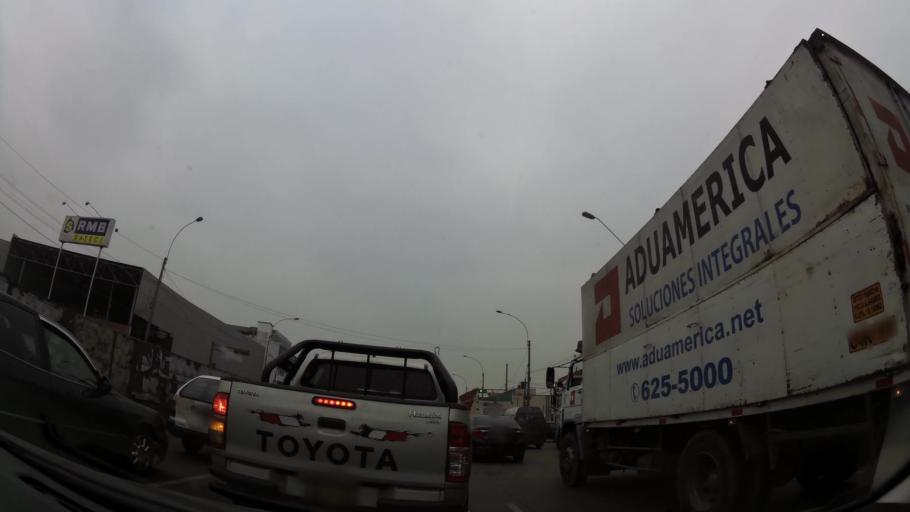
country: PE
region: Lima
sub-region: Lima
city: San Luis
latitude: -12.0601
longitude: -76.9768
